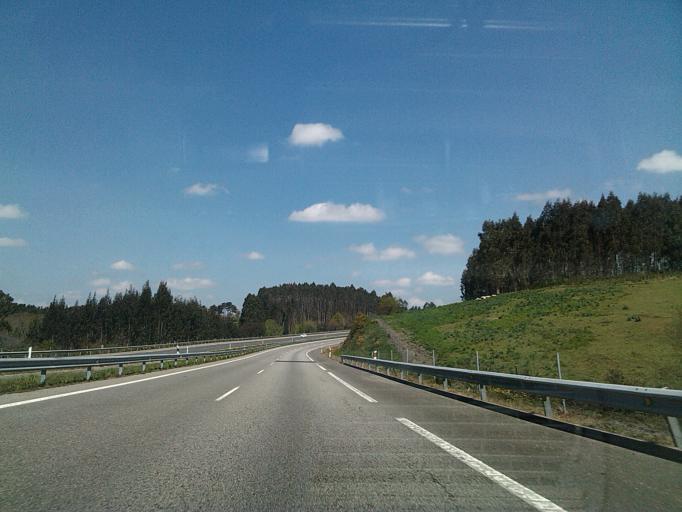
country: ES
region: Galicia
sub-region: Provincia da Coruna
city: Oroso
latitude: 42.9074
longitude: -8.4624
